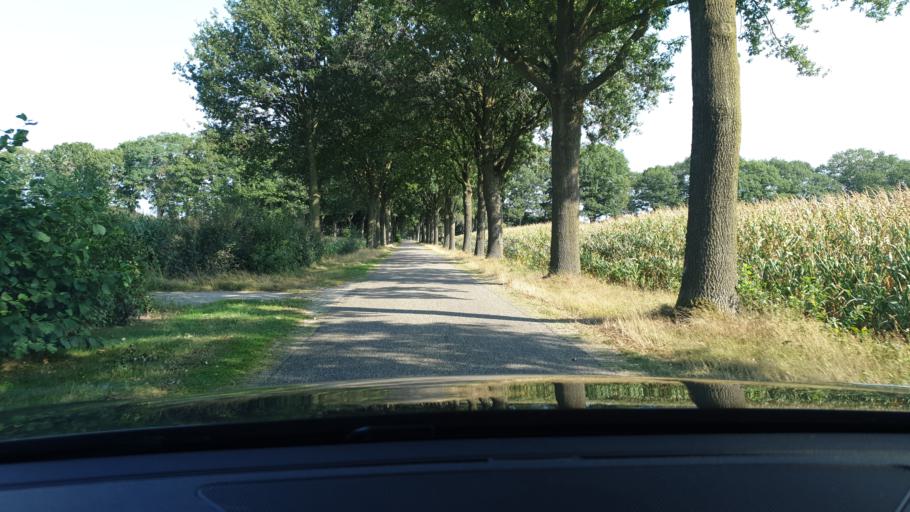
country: NL
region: North Brabant
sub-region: Gemeente Bernheze
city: Loosbroek
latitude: 51.6782
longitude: 5.4640
